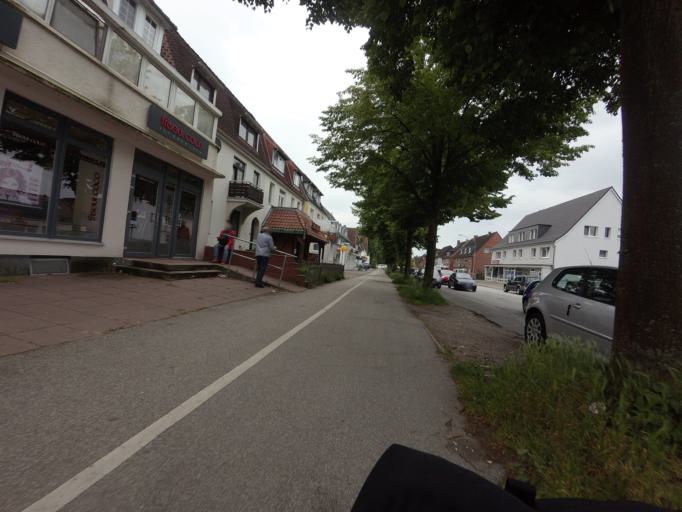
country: DE
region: Mecklenburg-Vorpommern
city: Selmsdorf
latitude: 53.9117
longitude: 10.8047
